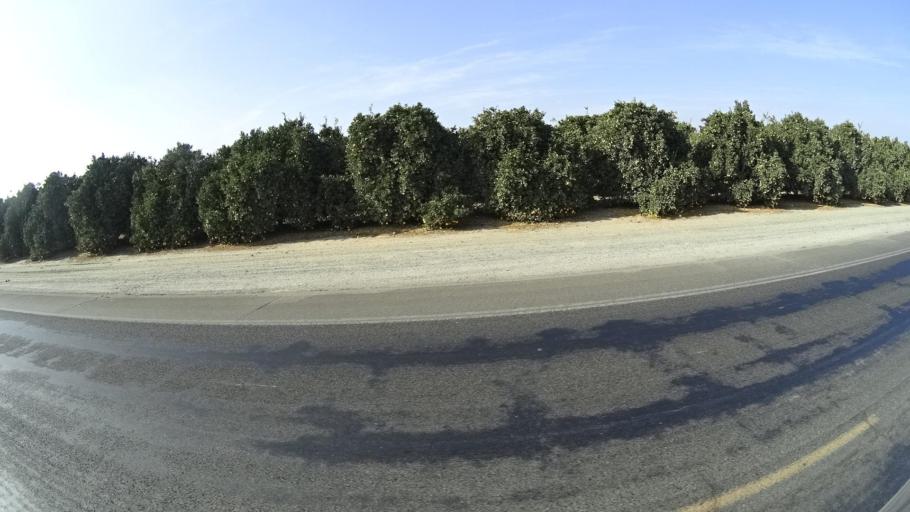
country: US
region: California
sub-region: Kern County
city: McFarland
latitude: 35.6919
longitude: -119.1757
